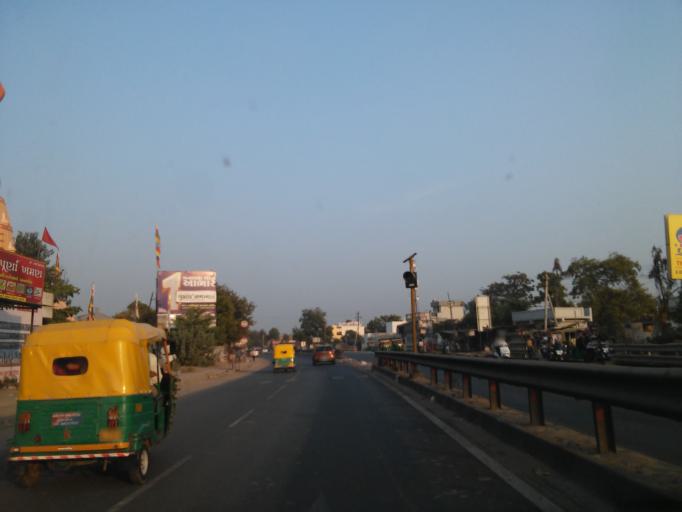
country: IN
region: Gujarat
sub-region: Ahmadabad
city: Sanand
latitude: 22.9847
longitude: 72.4349
